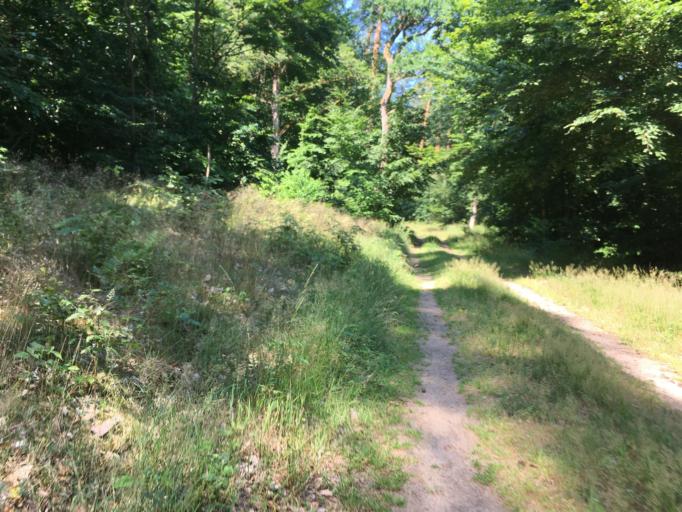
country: DE
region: Brandenburg
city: Marienwerder
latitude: 52.9149
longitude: 13.6401
